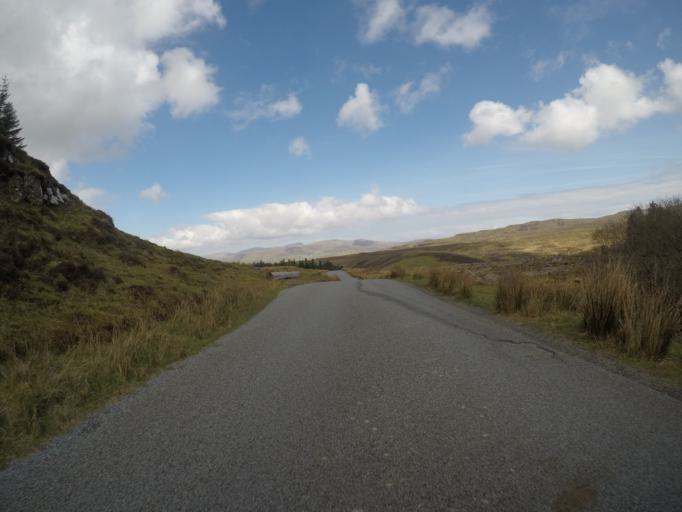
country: GB
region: Scotland
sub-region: Highland
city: Isle of Skye
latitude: 57.4103
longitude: -6.3040
